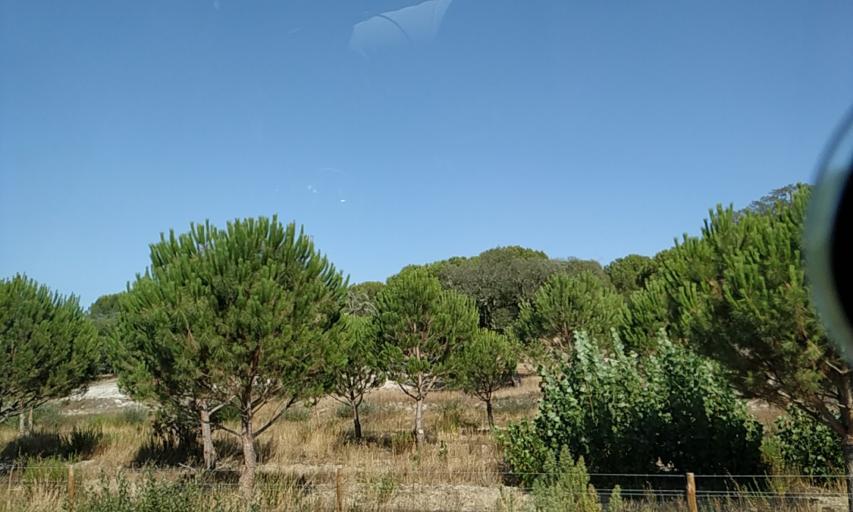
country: PT
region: Evora
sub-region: Vendas Novas
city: Vendas Novas
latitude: 38.7851
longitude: -8.5837
